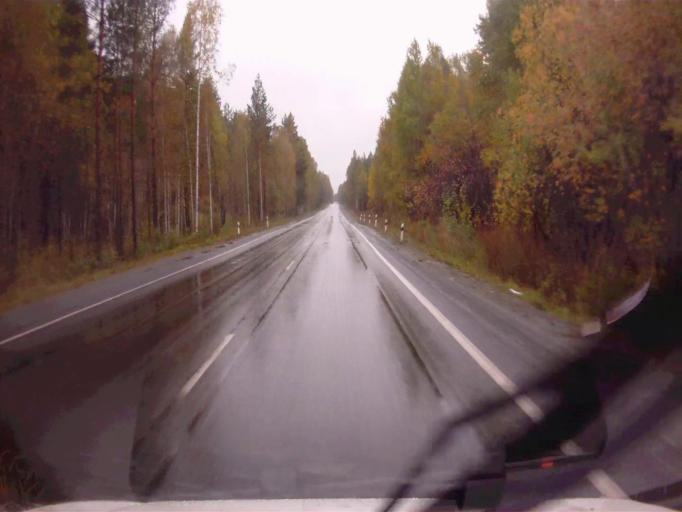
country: RU
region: Chelyabinsk
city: Tayginka
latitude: 55.5798
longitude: 60.6420
